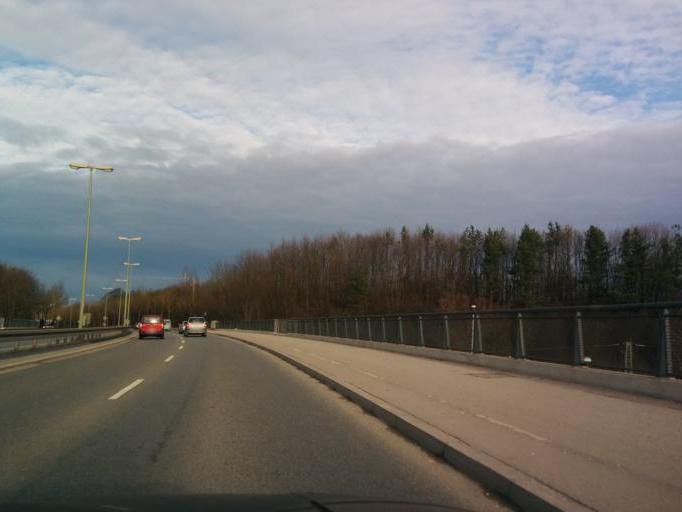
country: DE
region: Bavaria
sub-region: Upper Bavaria
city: Karlsfeld
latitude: 48.1978
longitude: 11.4947
